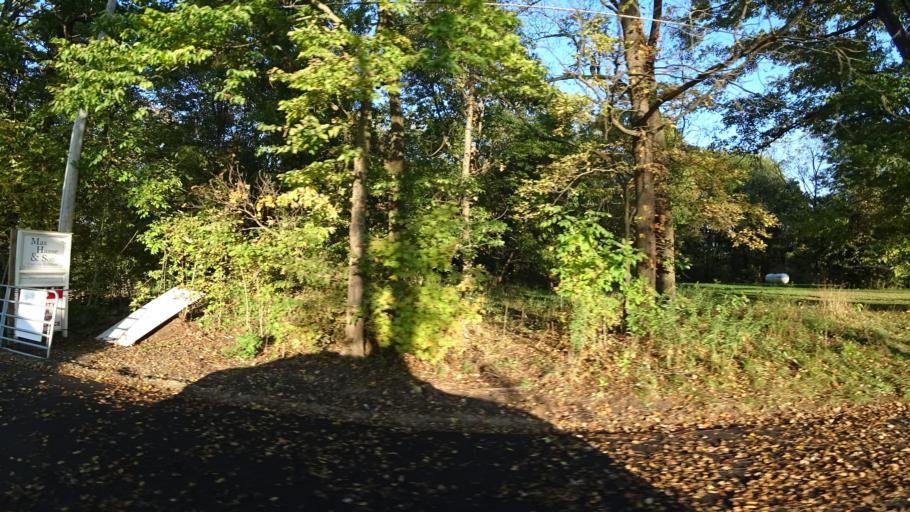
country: US
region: Michigan
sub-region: Saint Joseph County
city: Three Rivers
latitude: 41.9507
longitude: -85.6431
